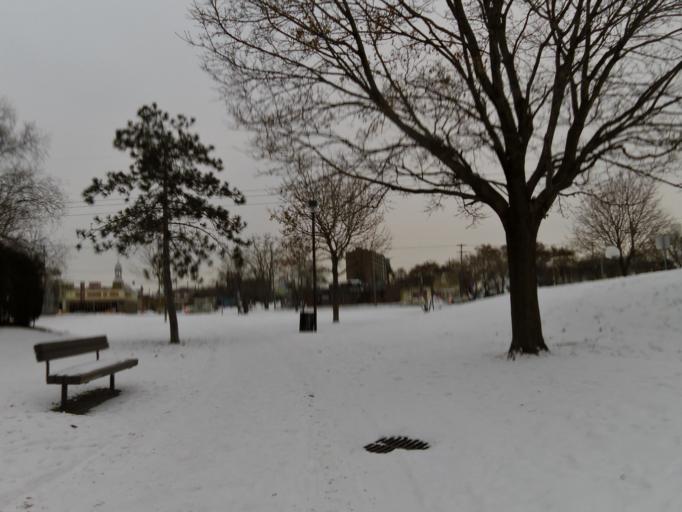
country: CA
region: Ontario
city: Ottawa
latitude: 45.4259
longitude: -75.6349
